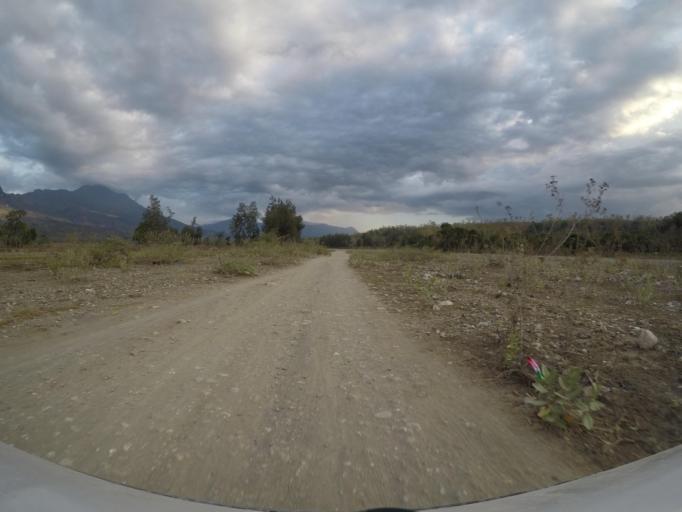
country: TL
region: Bobonaro
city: Maliana
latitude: -8.9013
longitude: 125.2091
